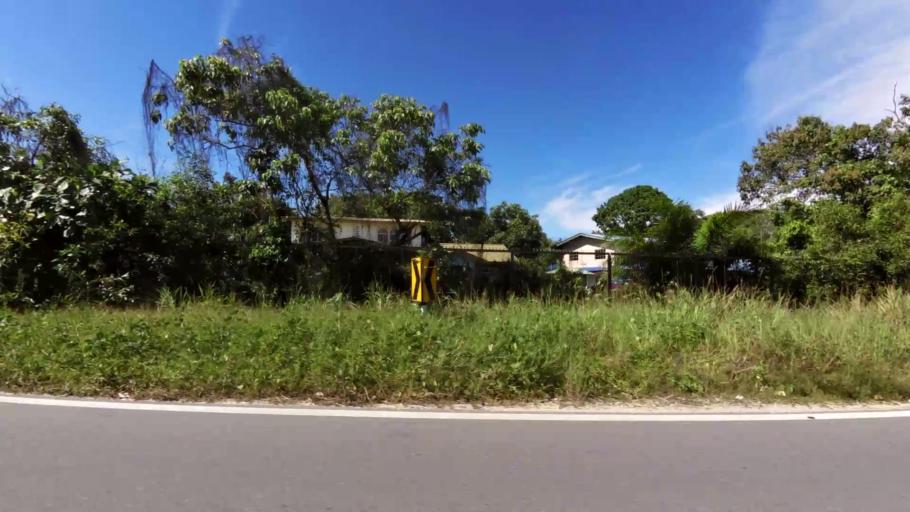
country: BN
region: Brunei and Muara
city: Bandar Seri Begawan
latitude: 5.0047
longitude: 115.0568
